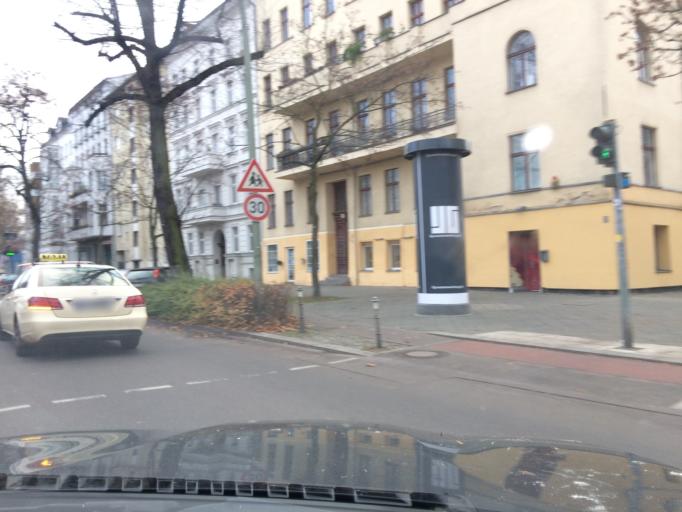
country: DE
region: Berlin
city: Moabit
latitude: 52.5310
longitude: 13.3519
